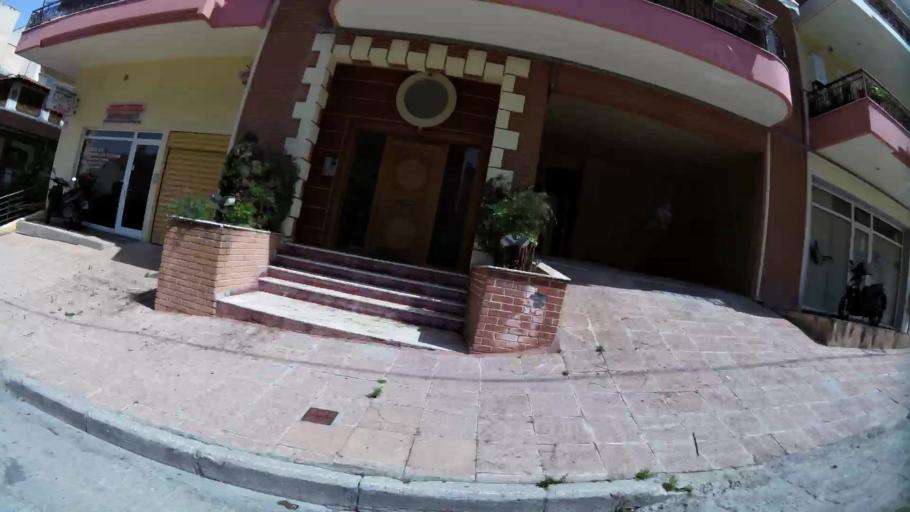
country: GR
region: Central Macedonia
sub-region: Nomos Thessalonikis
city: Evosmos
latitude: 40.6707
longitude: 22.9217
